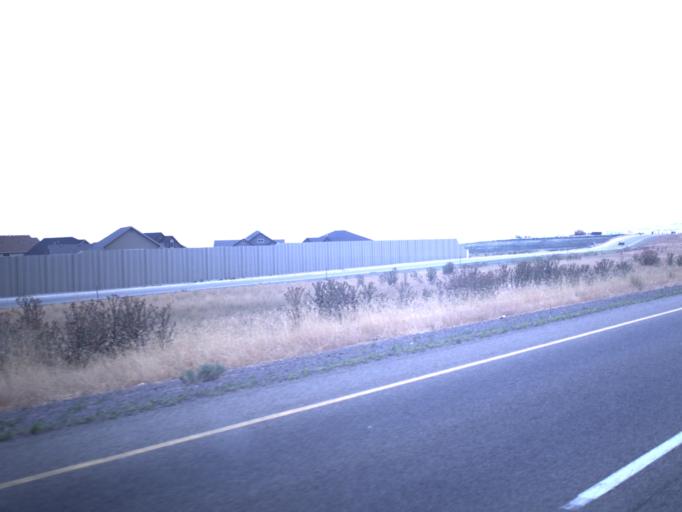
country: US
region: Utah
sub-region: Salt Lake County
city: Herriman
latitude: 40.5168
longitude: -112.0058
